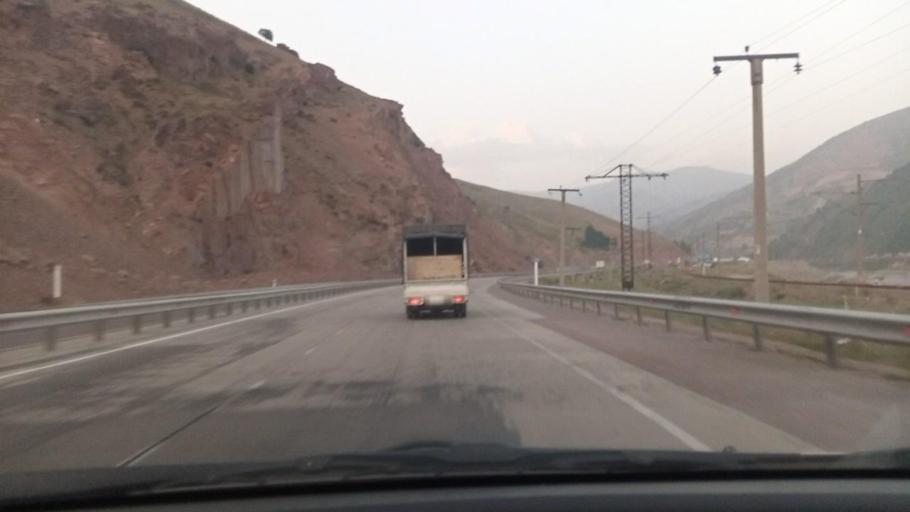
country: UZ
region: Toshkent
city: Angren
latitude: 41.1492
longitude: 70.4195
